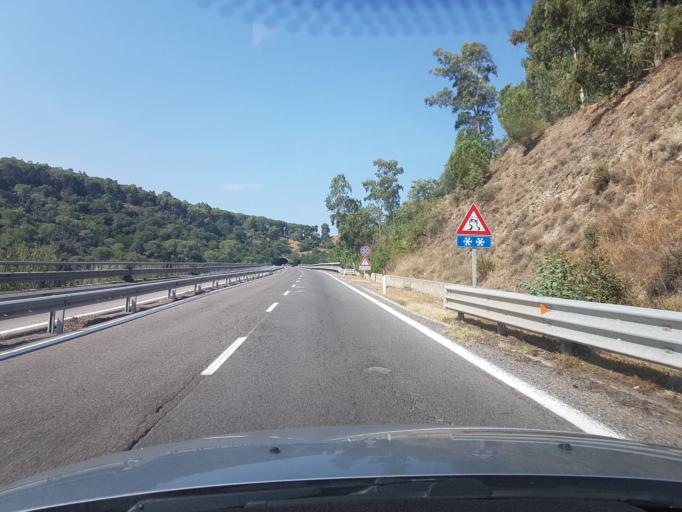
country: IT
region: Sardinia
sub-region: Provincia di Nuoro
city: Nuoro
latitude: 40.3328
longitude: 9.2946
